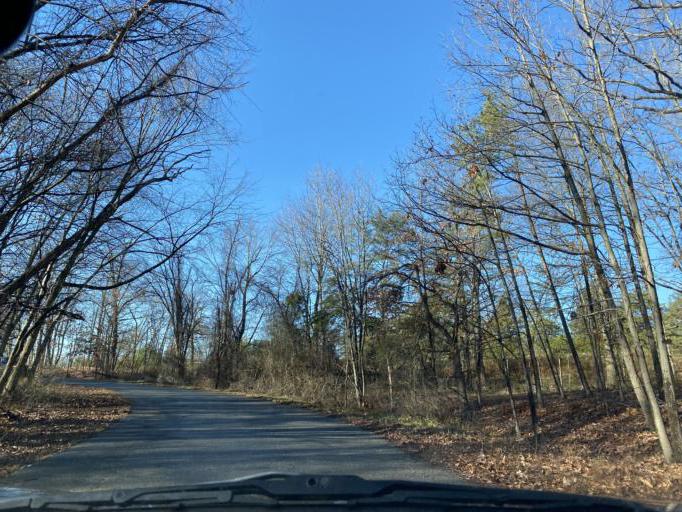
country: US
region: Maryland
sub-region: Prince George's County
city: West Laurel
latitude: 39.0980
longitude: -76.8857
